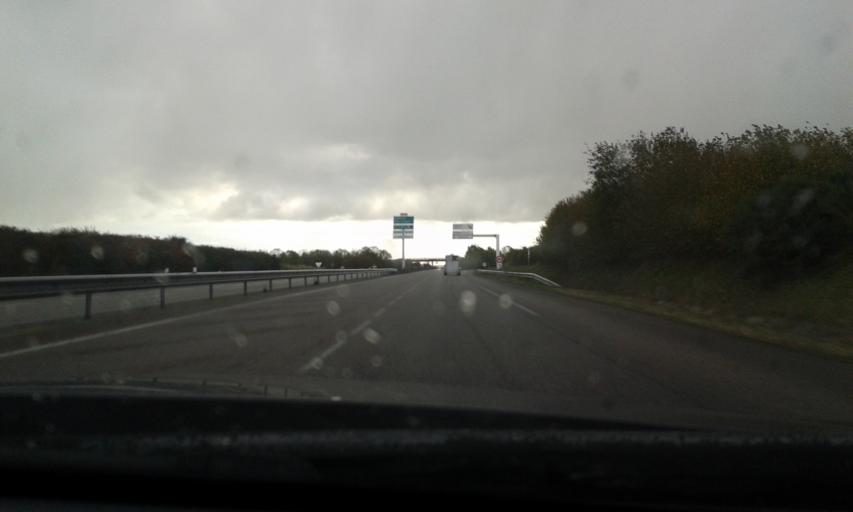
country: FR
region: Haute-Normandie
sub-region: Departement de l'Eure
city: Damville
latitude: 48.8926
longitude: 1.1718
